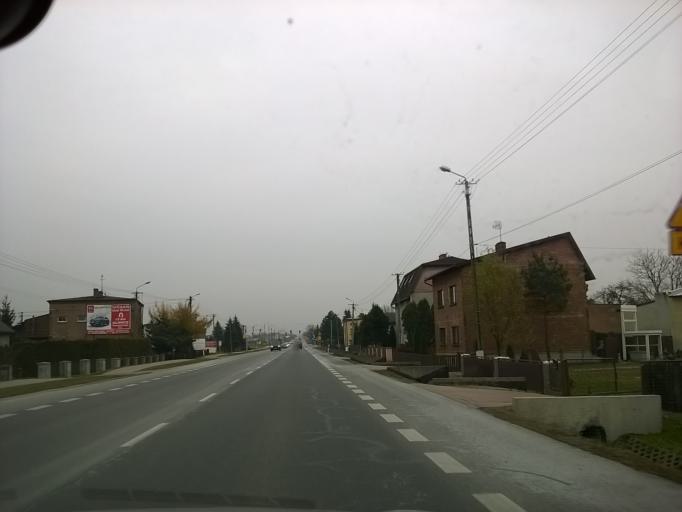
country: PL
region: Silesian Voivodeship
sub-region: Powiat gliwicki
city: Paniowki
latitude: 50.2405
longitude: 18.7669
